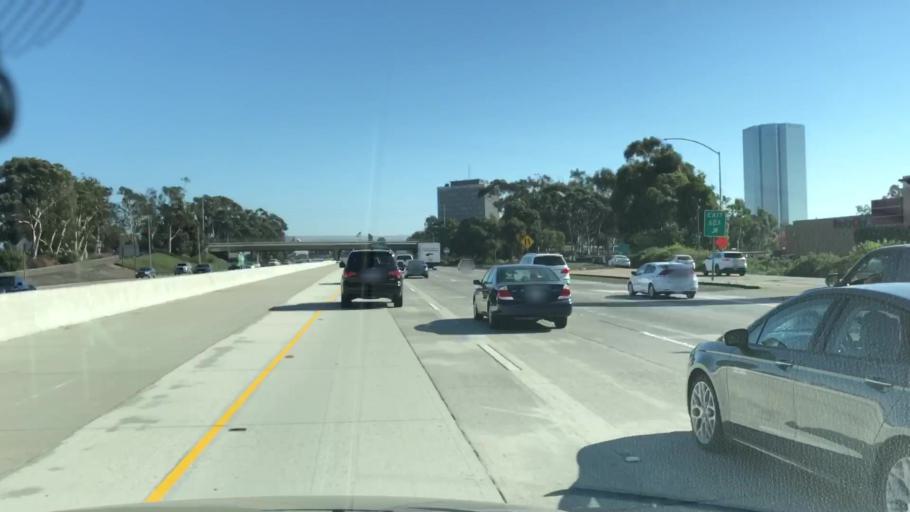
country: US
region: California
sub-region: Ventura County
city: El Rio
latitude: 34.2342
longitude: -119.1750
